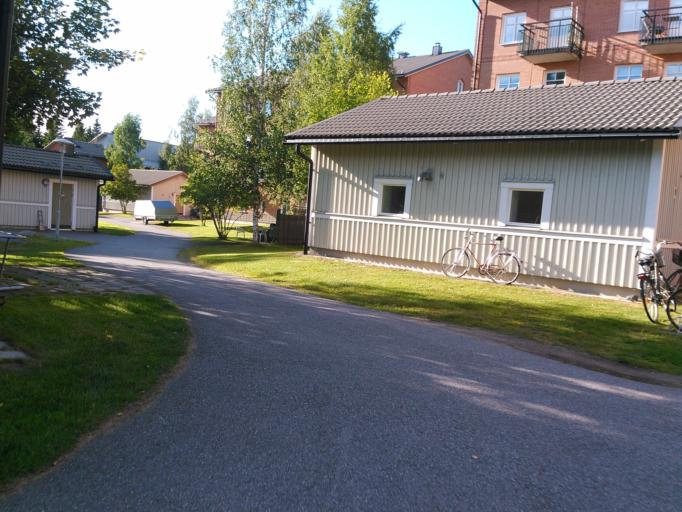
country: SE
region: Vaesterbotten
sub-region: Umea Kommun
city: Ersmark
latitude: 63.8264
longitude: 20.3260
